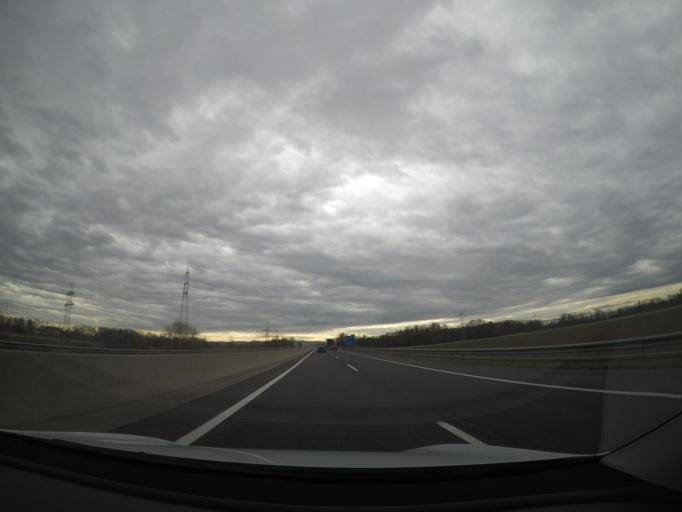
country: AT
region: Lower Austria
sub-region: Politischer Bezirk Baden
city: Ebreichsdorf
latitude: 47.9373
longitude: 16.3790
